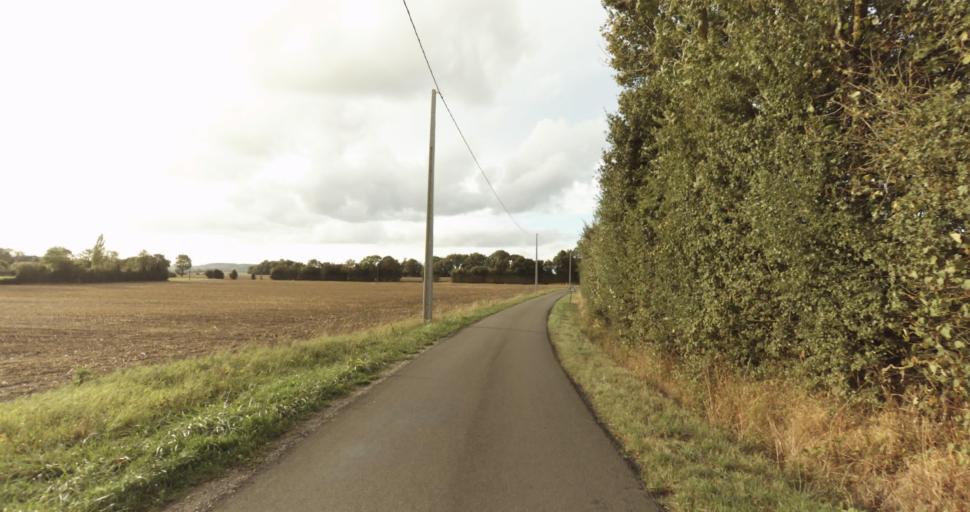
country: FR
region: Lower Normandy
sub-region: Departement de l'Orne
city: Sees
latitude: 48.6907
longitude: 0.2451
